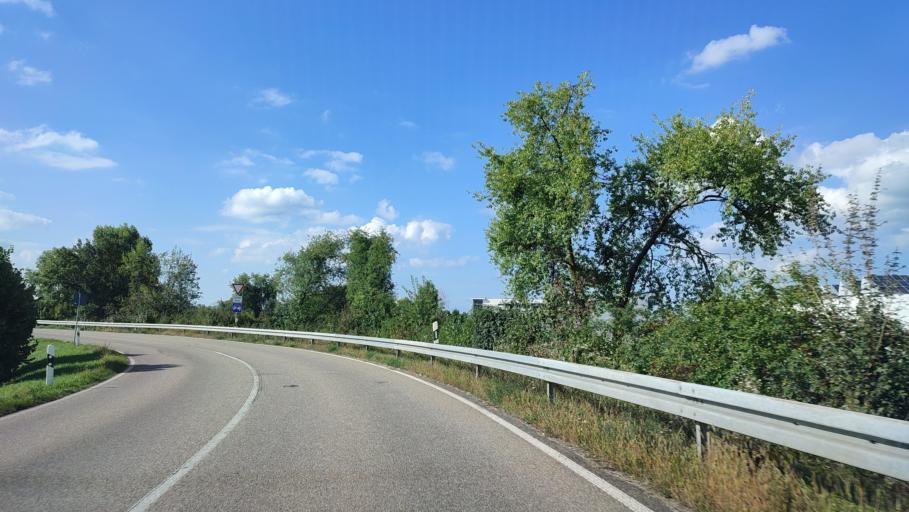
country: DE
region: Baden-Wuerttemberg
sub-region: Freiburg Region
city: Appenweier
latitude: 48.5410
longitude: 8.0201
